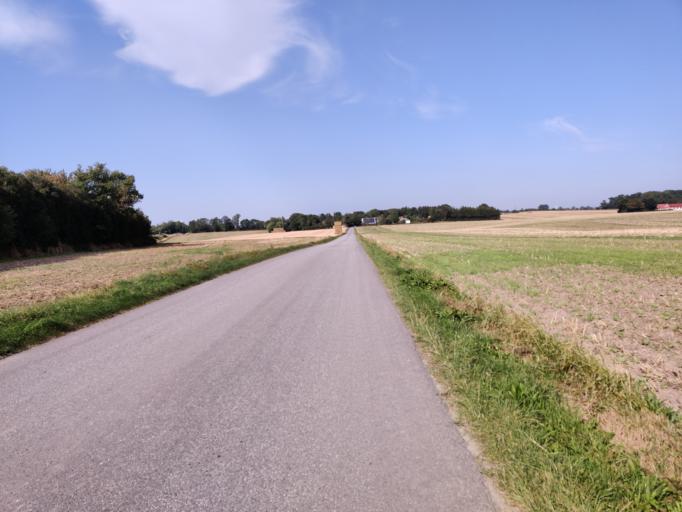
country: DK
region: Zealand
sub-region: Guldborgsund Kommune
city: Nykobing Falster
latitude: 54.6934
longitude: 11.9030
